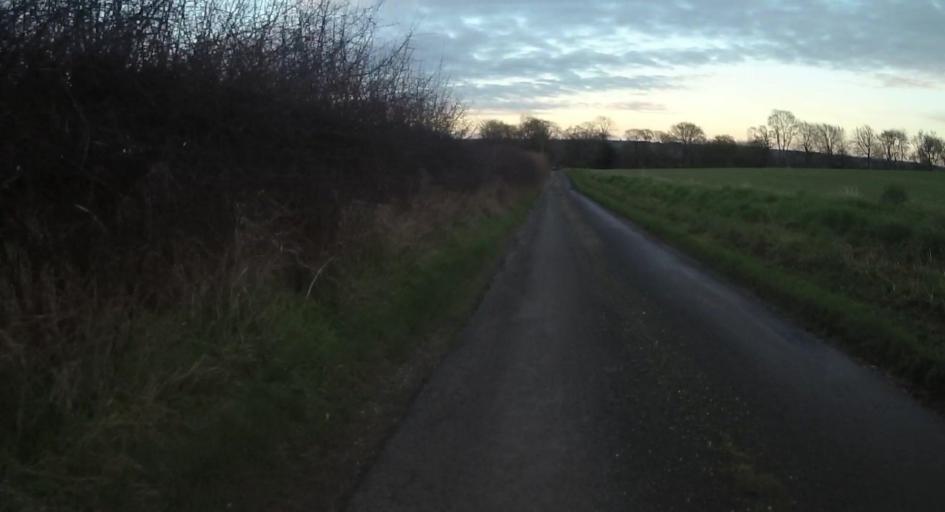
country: GB
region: England
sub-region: Hampshire
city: Swanmore
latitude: 51.0168
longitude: -1.1380
